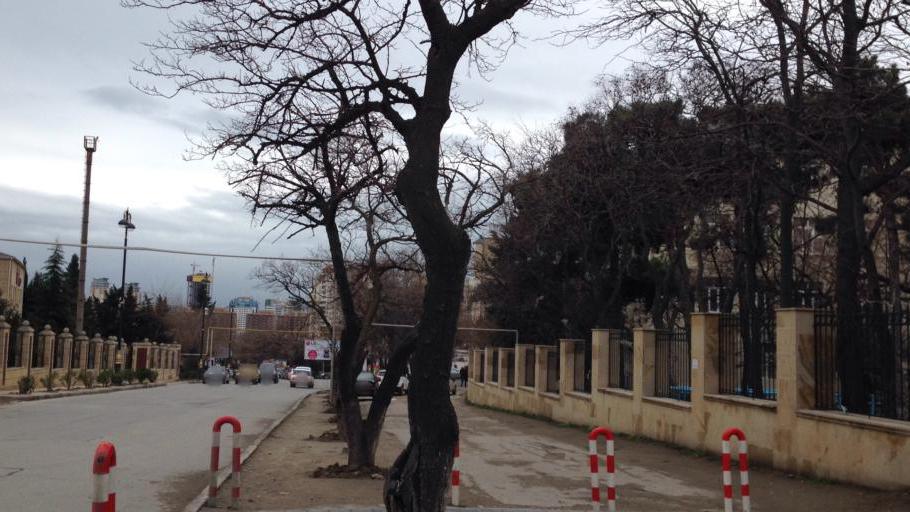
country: AZ
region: Baki
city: Baku
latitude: 40.3904
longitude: 49.8495
